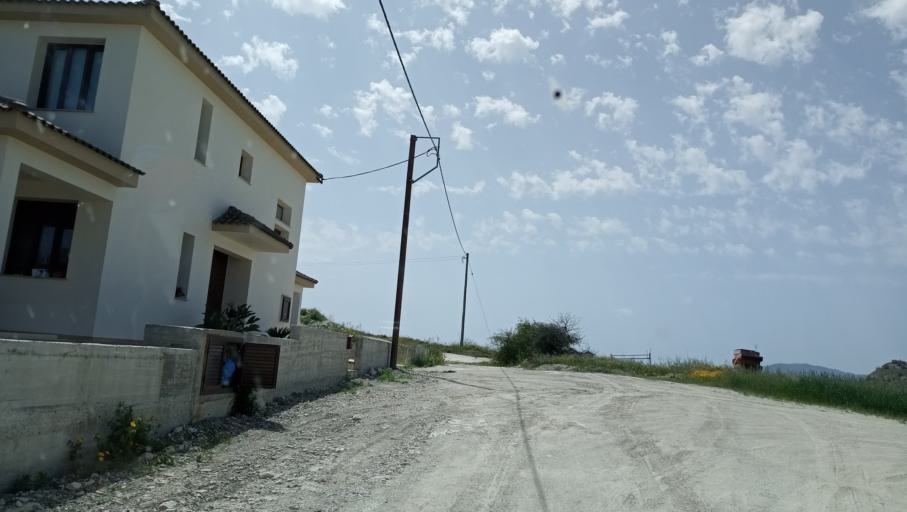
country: CY
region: Lefkosia
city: Dali
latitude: 35.0124
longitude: 33.4212
